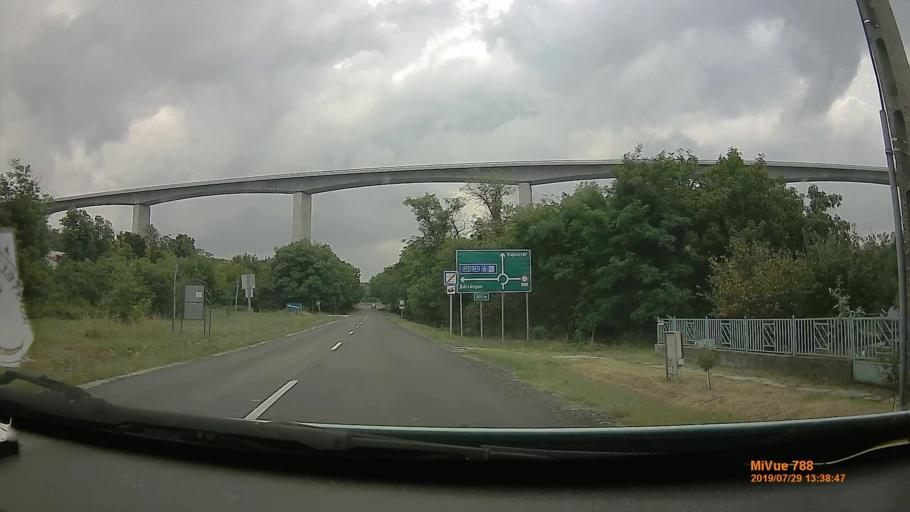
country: HU
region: Somogy
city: Balatonfoldvar
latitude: 46.8192
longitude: 17.9067
